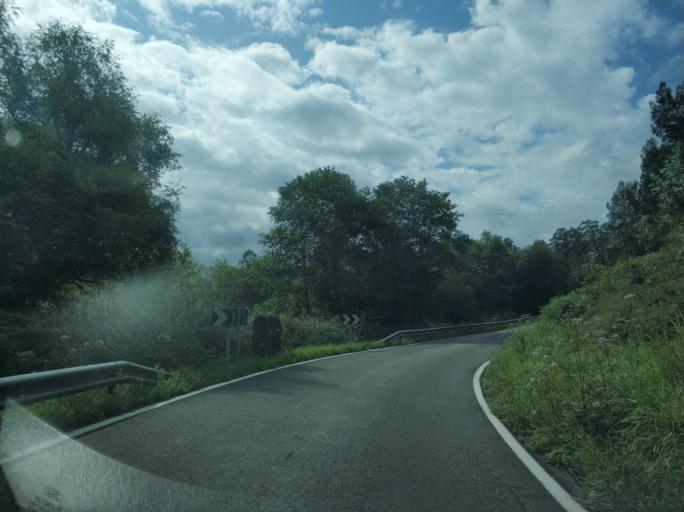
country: ES
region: Cantabria
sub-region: Provincia de Cantabria
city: Polanco
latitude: 43.3767
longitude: -3.9713
